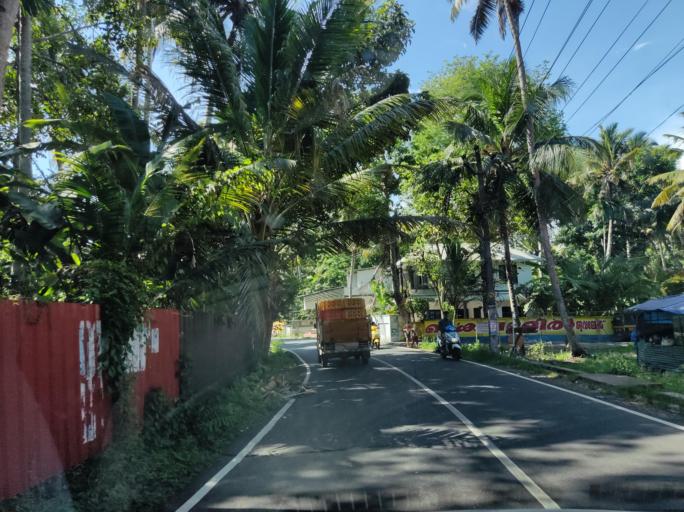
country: IN
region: Kerala
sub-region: Alappuzha
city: Kayankulam
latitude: 9.2735
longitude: 76.4017
